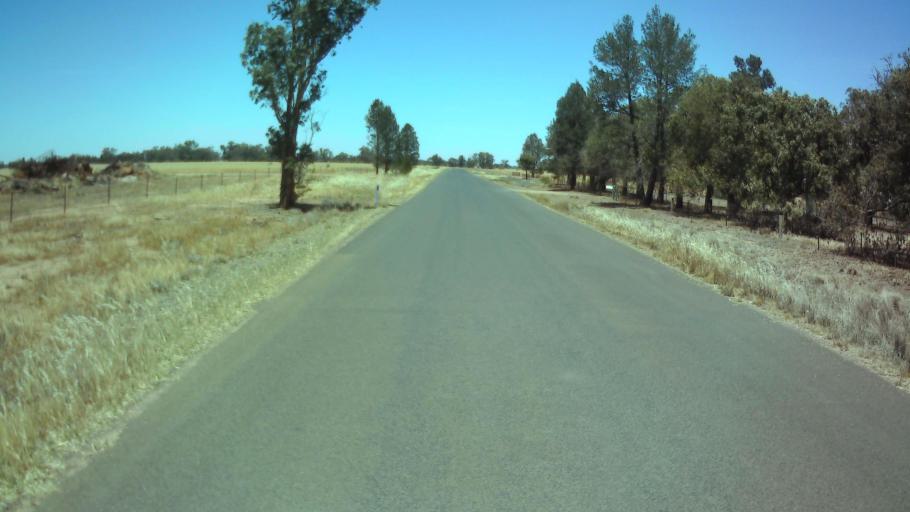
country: AU
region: New South Wales
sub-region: Weddin
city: Grenfell
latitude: -34.0315
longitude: 147.7907
